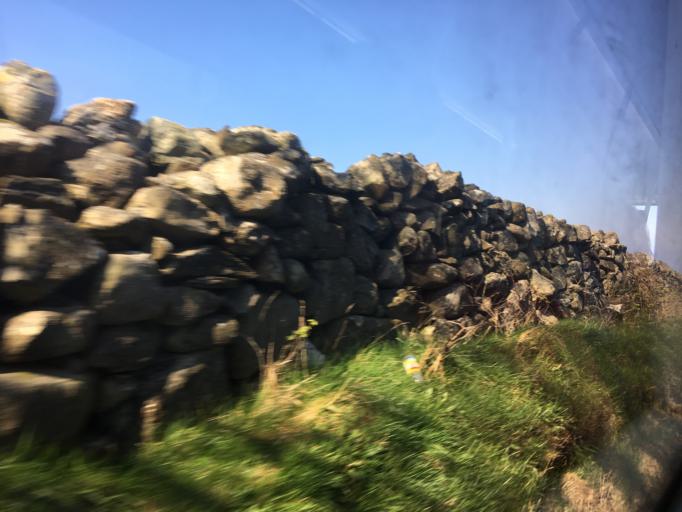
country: GB
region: Wales
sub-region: Gwynedd
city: Llanwnda
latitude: 53.0310
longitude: -4.2855
